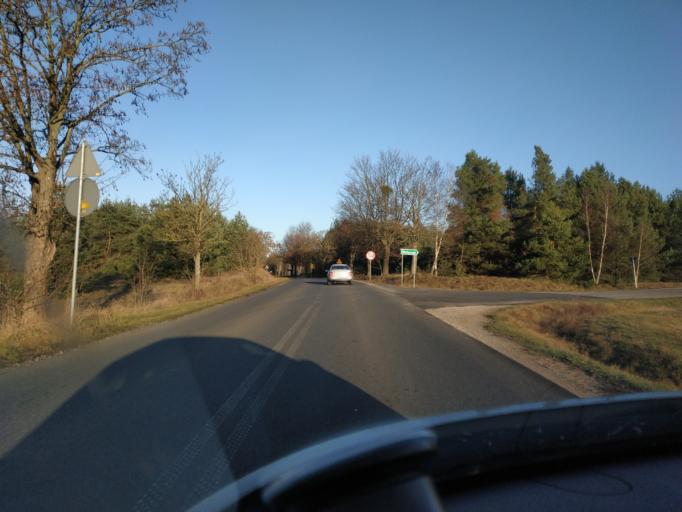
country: PL
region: Kujawsko-Pomorskie
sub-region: Powiat wabrzeski
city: Wabrzezno
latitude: 53.2308
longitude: 18.9548
